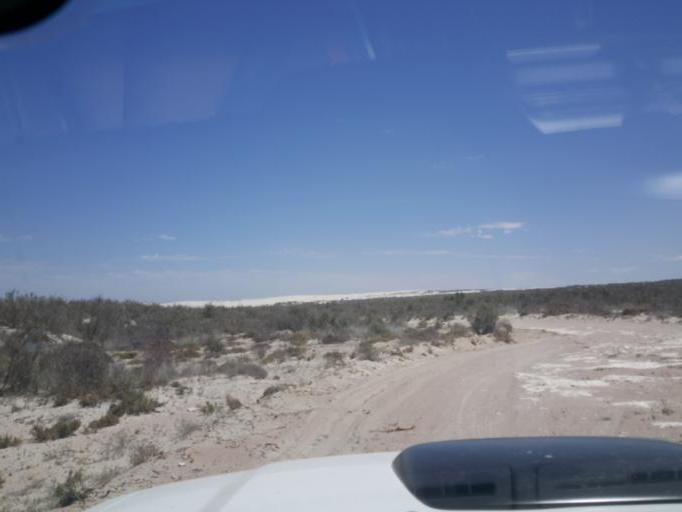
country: ZA
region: Northern Cape
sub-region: Namakwa District Municipality
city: Garies
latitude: -30.5613
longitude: 17.4406
